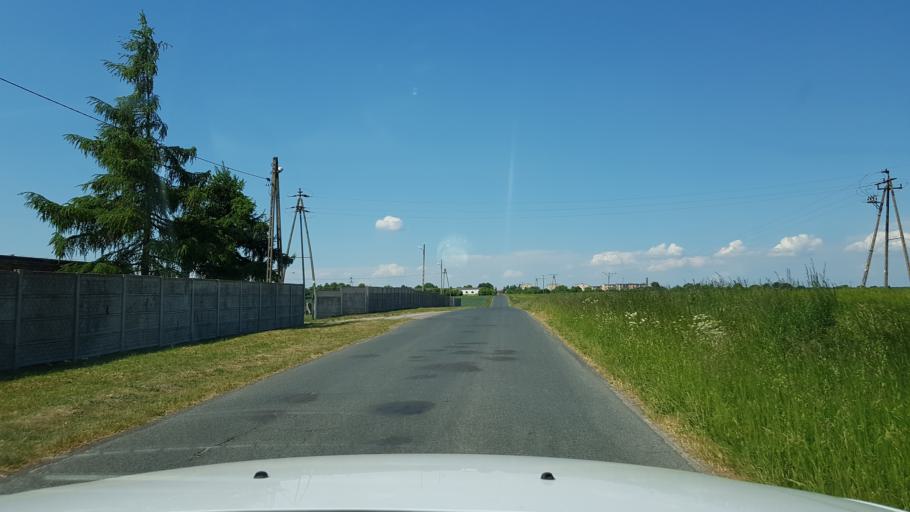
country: PL
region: West Pomeranian Voivodeship
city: Trzcinsko Zdroj
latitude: 53.0106
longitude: 14.5646
